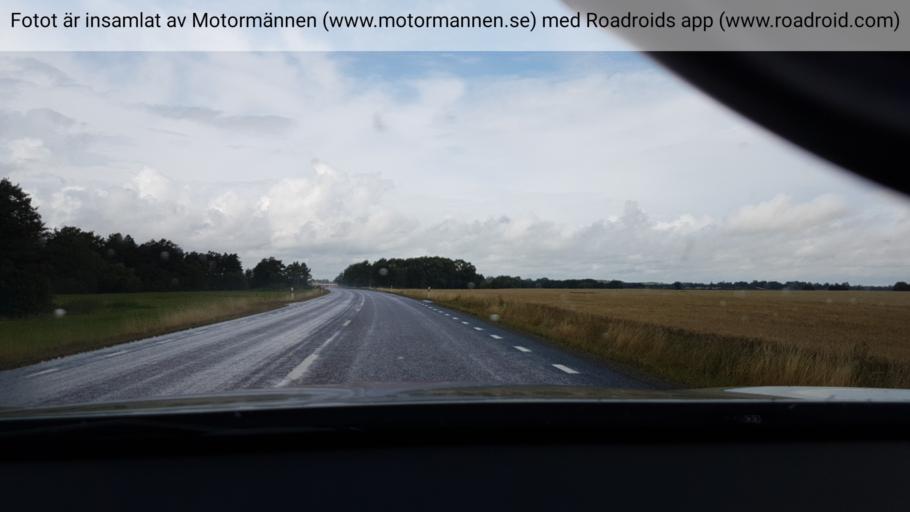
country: SE
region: Uppsala
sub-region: Uppsala Kommun
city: Gamla Uppsala
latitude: 59.9095
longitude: 17.5363
